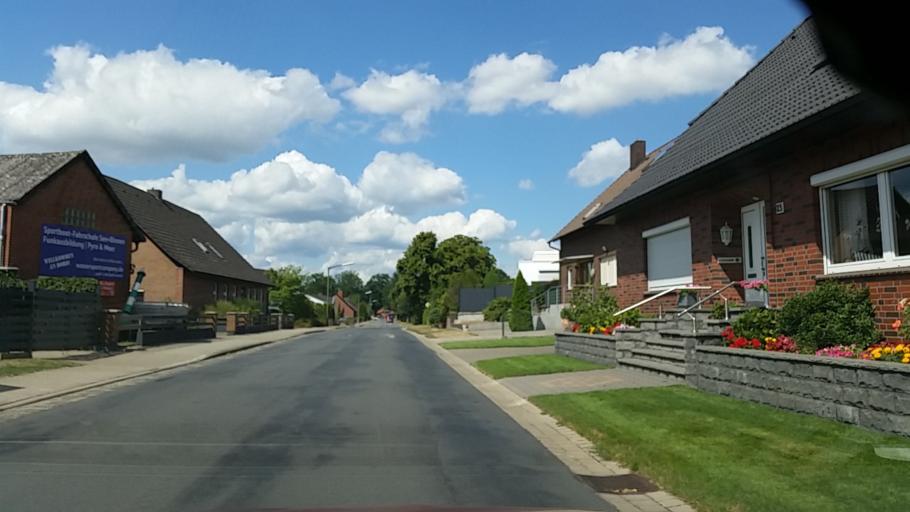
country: DE
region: Lower Saxony
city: Hankensbuttel
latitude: 52.7167
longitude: 10.6226
